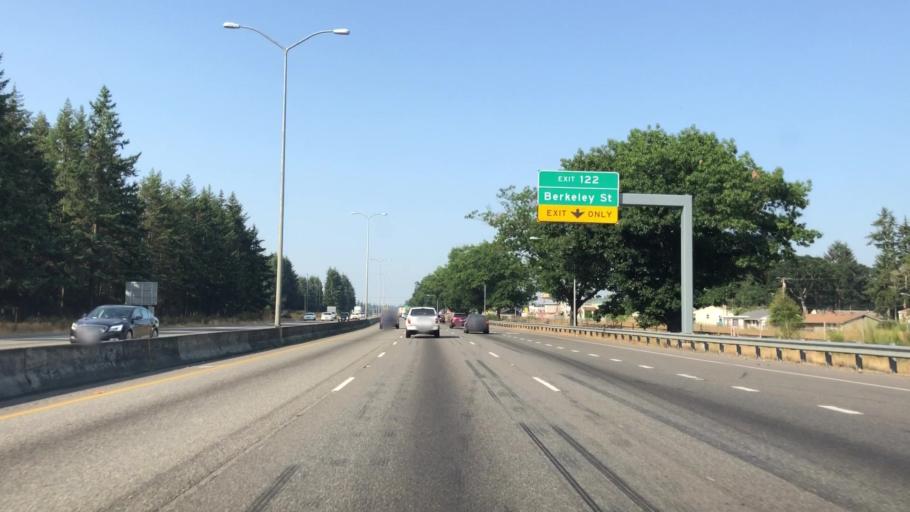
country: US
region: Washington
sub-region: Pierce County
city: Fort Lewis
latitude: 47.1249
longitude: -122.5465
